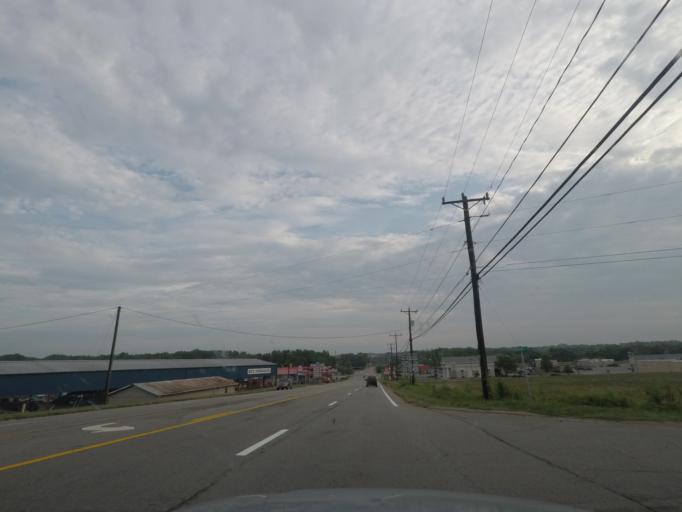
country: US
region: Virginia
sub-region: Halifax County
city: South Boston
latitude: 36.6846
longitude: -78.8993
